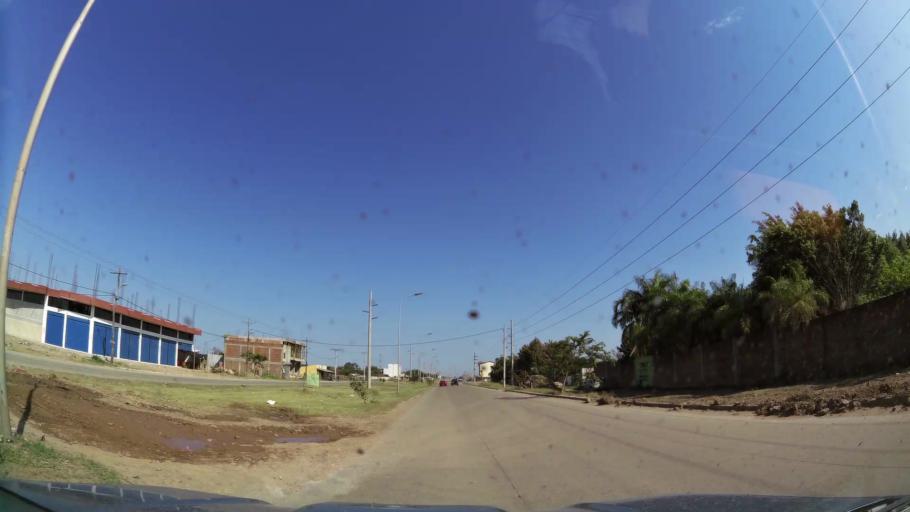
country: BO
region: Santa Cruz
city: Cotoca
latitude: -17.7846
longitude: -63.1083
